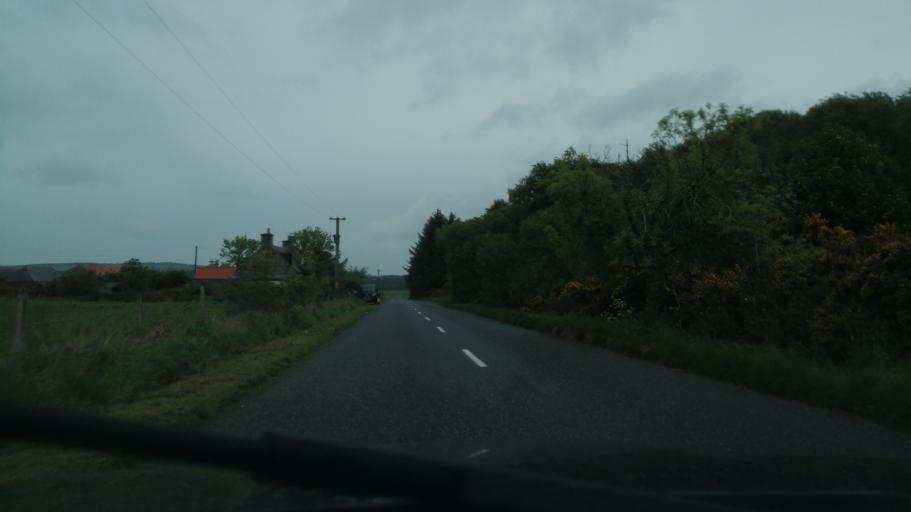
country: GB
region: Scotland
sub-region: Aberdeenshire
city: Portsoy
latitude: 57.6106
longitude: -2.7243
